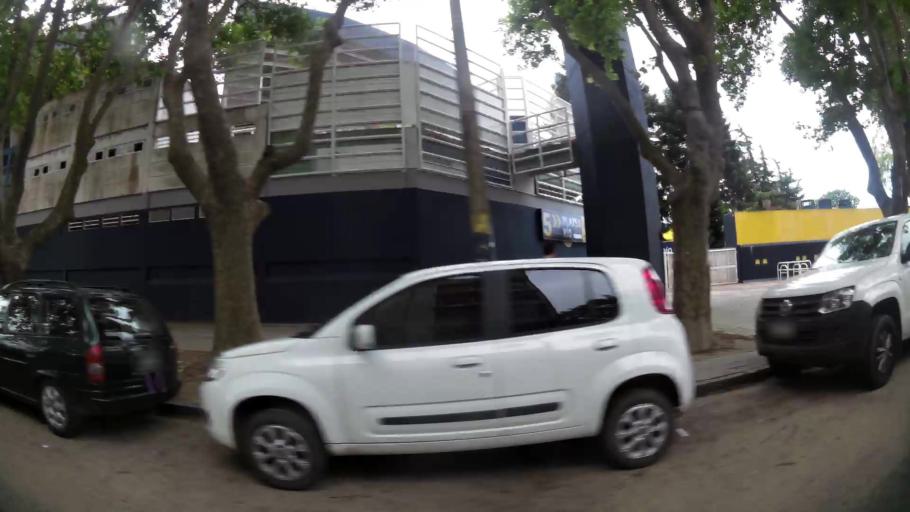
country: AR
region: Santa Fe
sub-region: Departamento de Rosario
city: Rosario
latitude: -32.9149
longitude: -60.6738
